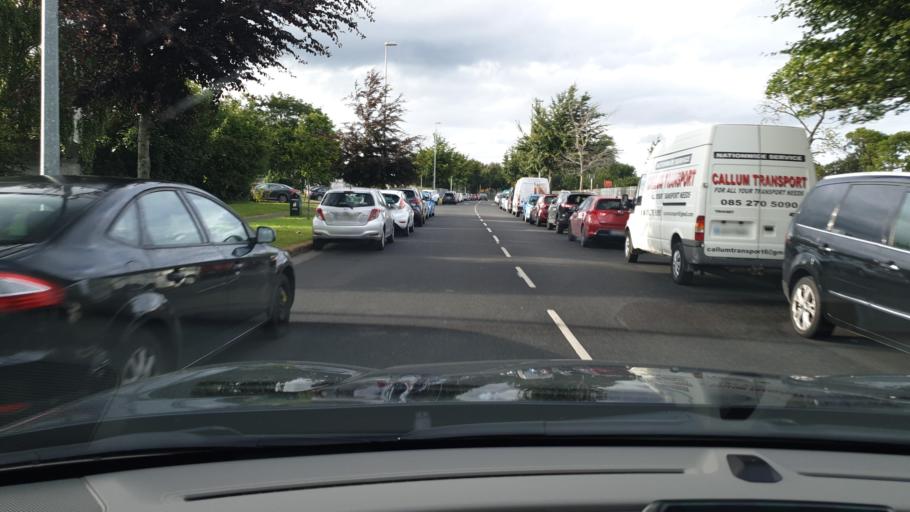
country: IE
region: Leinster
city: Clondalkin
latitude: 53.3388
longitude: -6.3944
